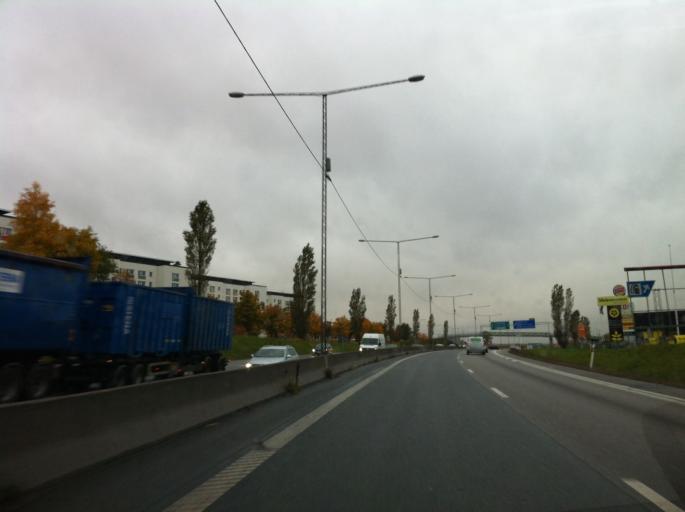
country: SE
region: Joenkoeping
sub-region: Jonkopings Kommun
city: Huskvarna
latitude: 57.7872
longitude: 14.2385
